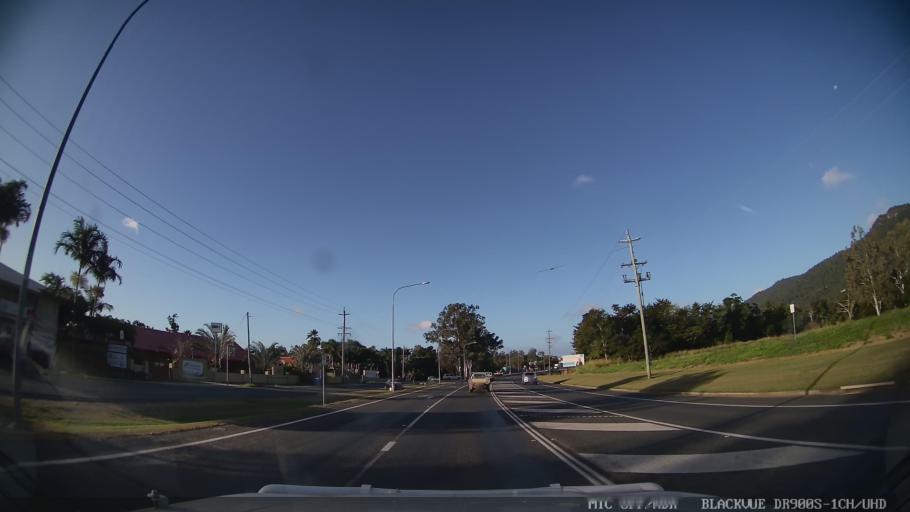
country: AU
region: Queensland
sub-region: Whitsunday
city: Proserpine
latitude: -20.2877
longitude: 148.6786
